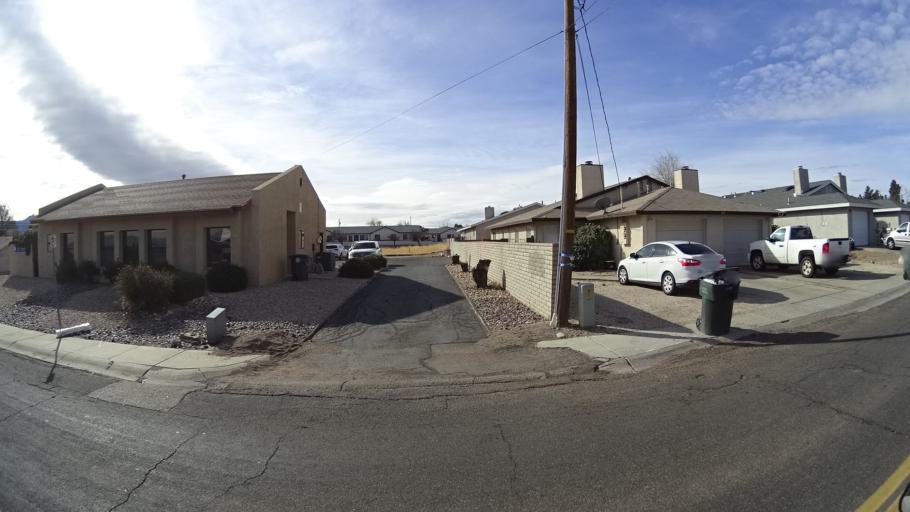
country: US
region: Arizona
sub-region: Mohave County
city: Kingman
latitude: 35.2222
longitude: -114.0429
